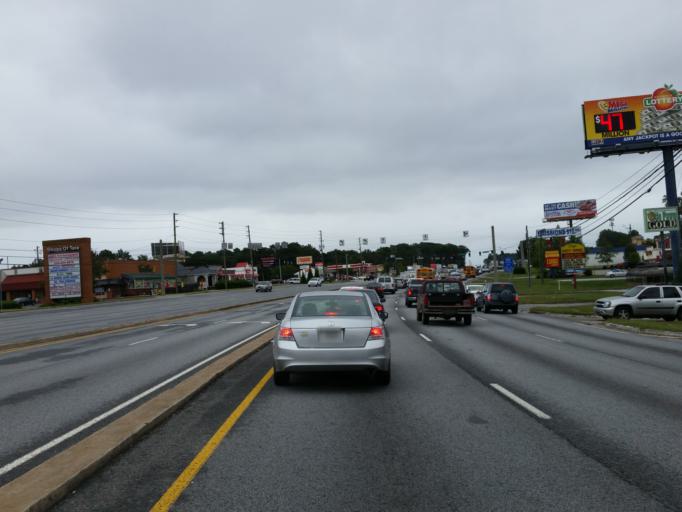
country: US
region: Georgia
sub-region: Clayton County
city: Morrow
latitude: 33.5753
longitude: -84.3721
